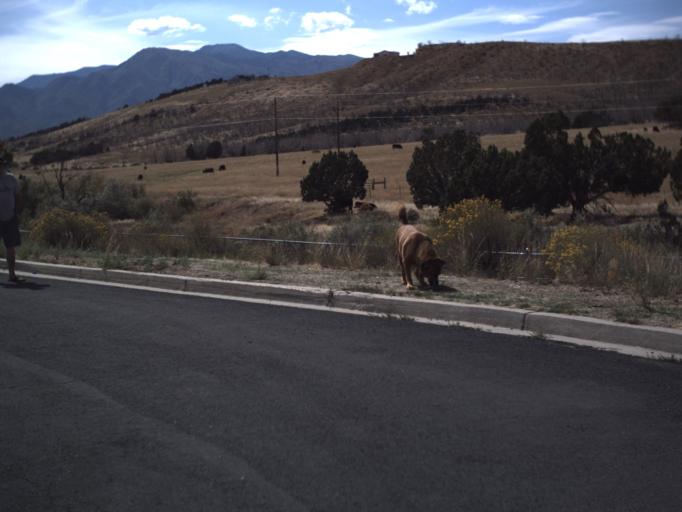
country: US
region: Utah
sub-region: Iron County
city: Cedar City
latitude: 37.5172
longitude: -113.2128
